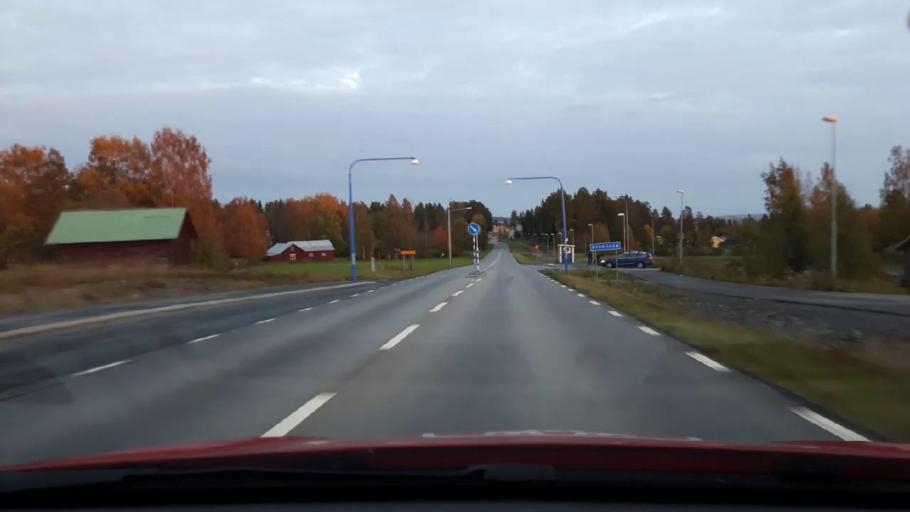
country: SE
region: Jaemtland
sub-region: OEstersunds Kommun
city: Ostersund
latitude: 63.2224
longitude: 14.6013
